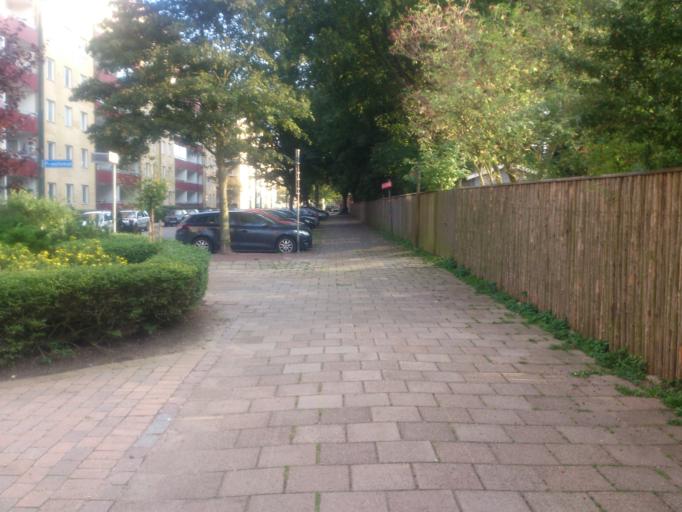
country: SE
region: Skane
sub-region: Malmo
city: Malmoe
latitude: 55.6013
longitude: 12.9710
